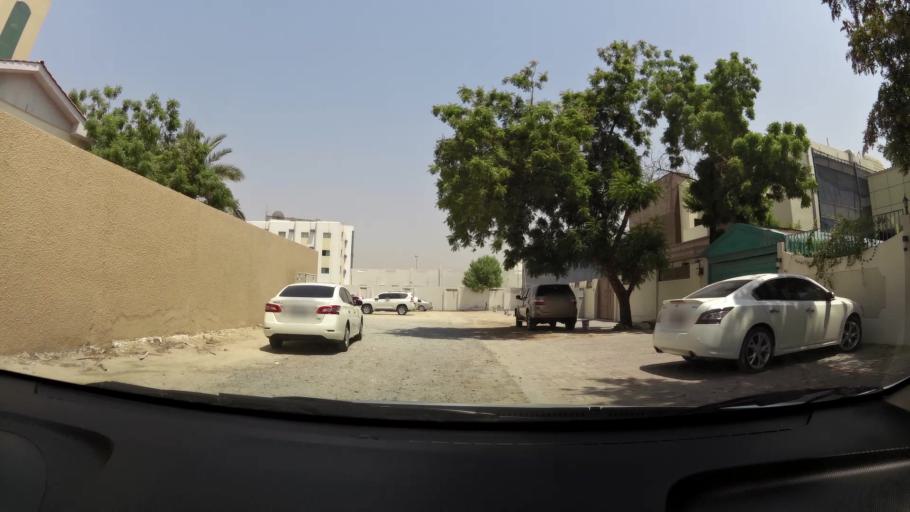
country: AE
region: Ajman
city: Ajman
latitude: 25.4024
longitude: 55.4362
